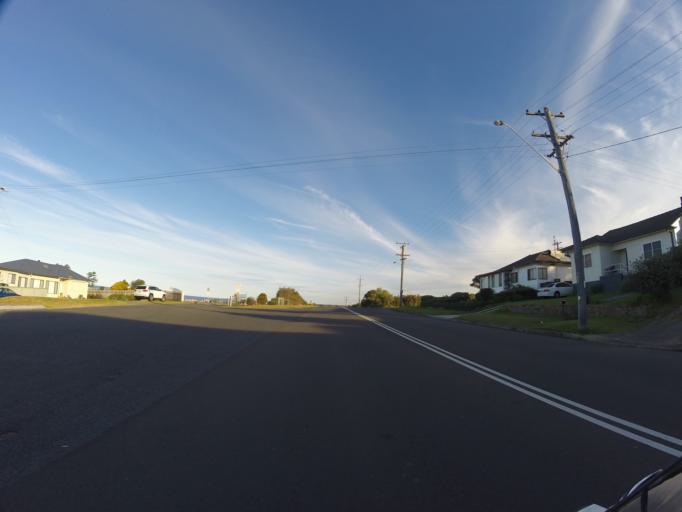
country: AU
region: New South Wales
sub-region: Wollongong
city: Bulli
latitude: -34.3403
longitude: 150.9203
